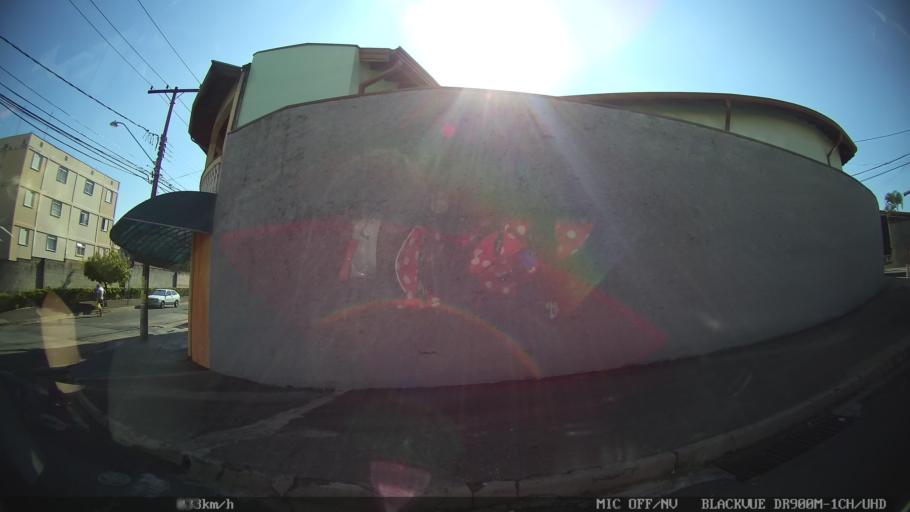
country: BR
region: Sao Paulo
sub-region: Campinas
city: Campinas
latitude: -22.9454
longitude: -47.1221
